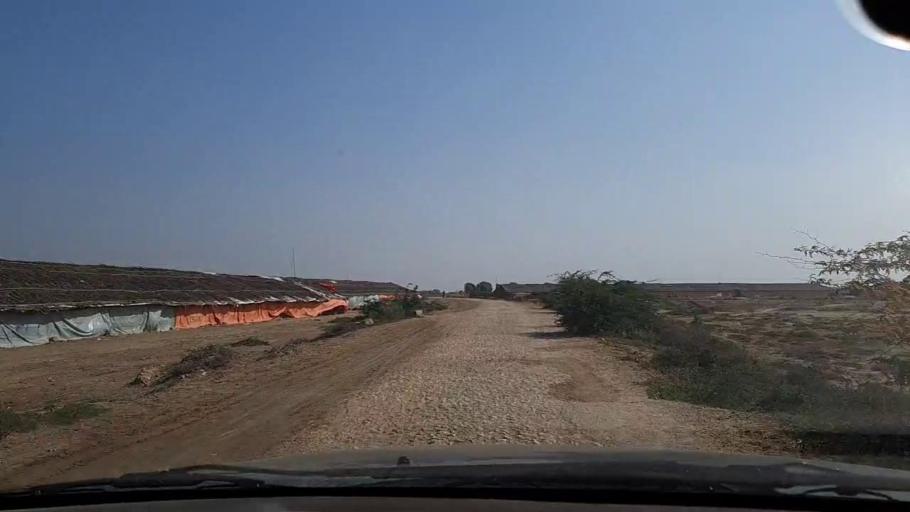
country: PK
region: Sindh
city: Chuhar Jamali
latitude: 24.4197
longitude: 67.8259
